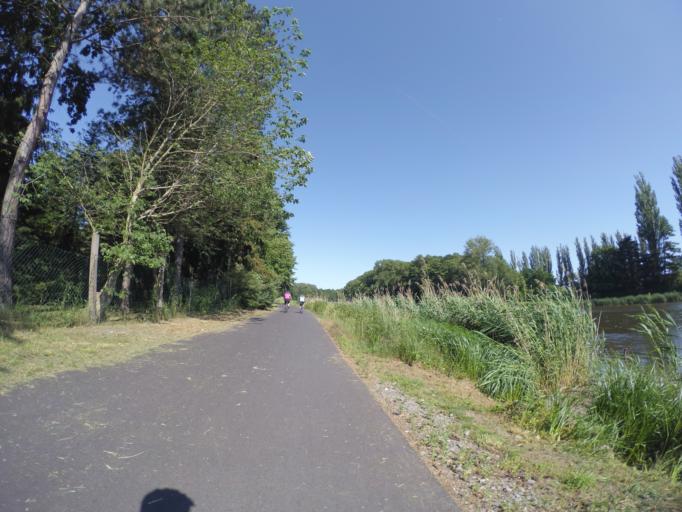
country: CZ
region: Central Bohemia
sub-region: Okres Nymburk
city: Nymburk
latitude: 50.1796
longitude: 15.0633
